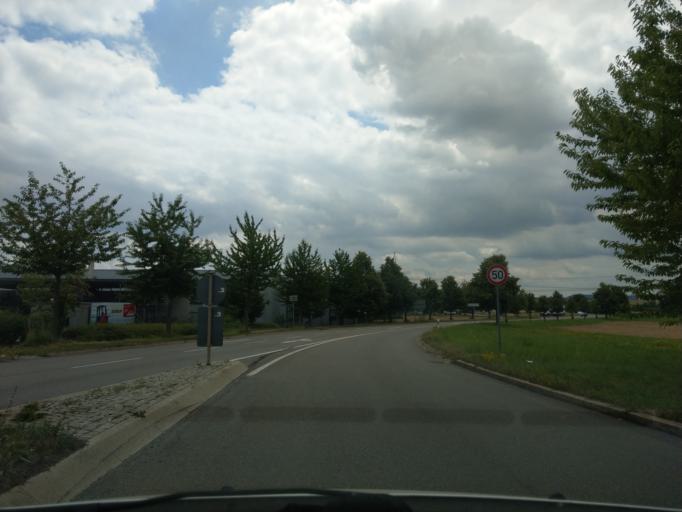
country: DE
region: Baden-Wuerttemberg
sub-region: Regierungsbezirk Stuttgart
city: Ostfildern
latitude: 48.7066
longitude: 9.2490
